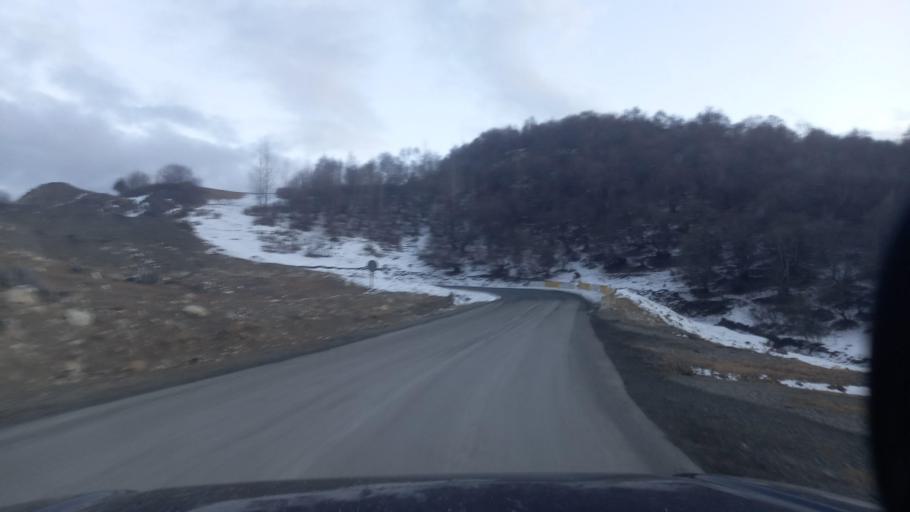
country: RU
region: Ingushetiya
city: Dzhayrakh
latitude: 42.8221
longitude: 44.8192
